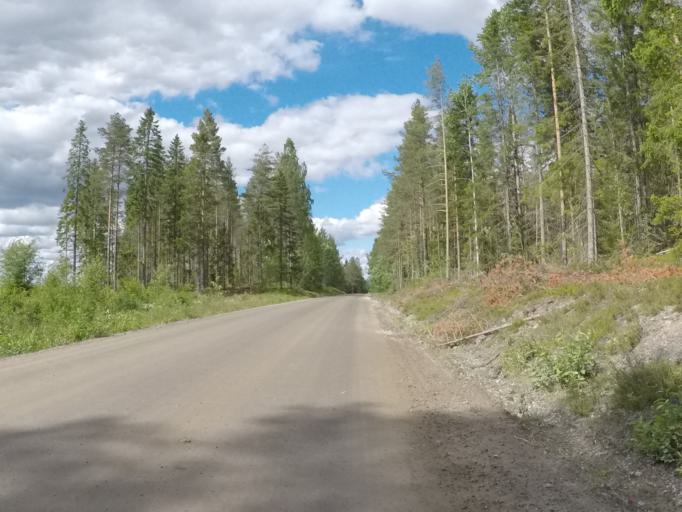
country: SE
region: Vaesterbotten
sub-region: Robertsfors Kommun
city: Robertsfors
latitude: 64.1357
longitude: 20.9025
